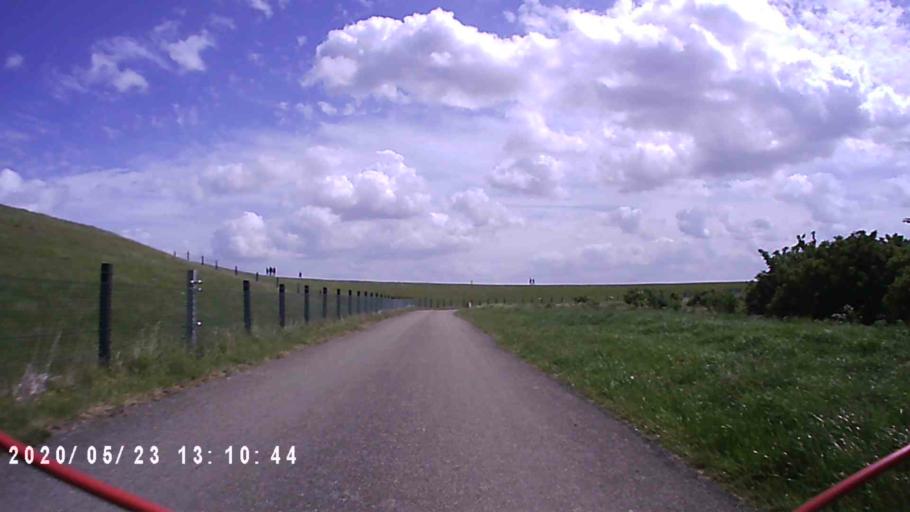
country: DE
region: Lower Saxony
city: Emden
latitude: 53.3010
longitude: 7.0812
